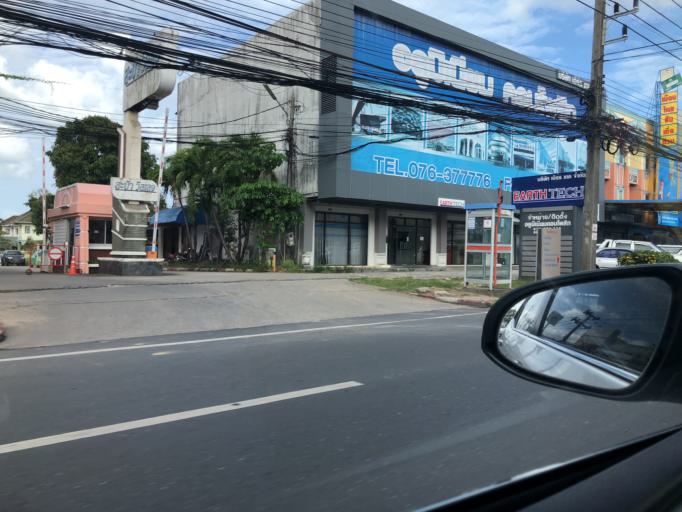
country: TH
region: Phuket
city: Ban Ko Kaeo
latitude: 7.9450
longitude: 98.3933
